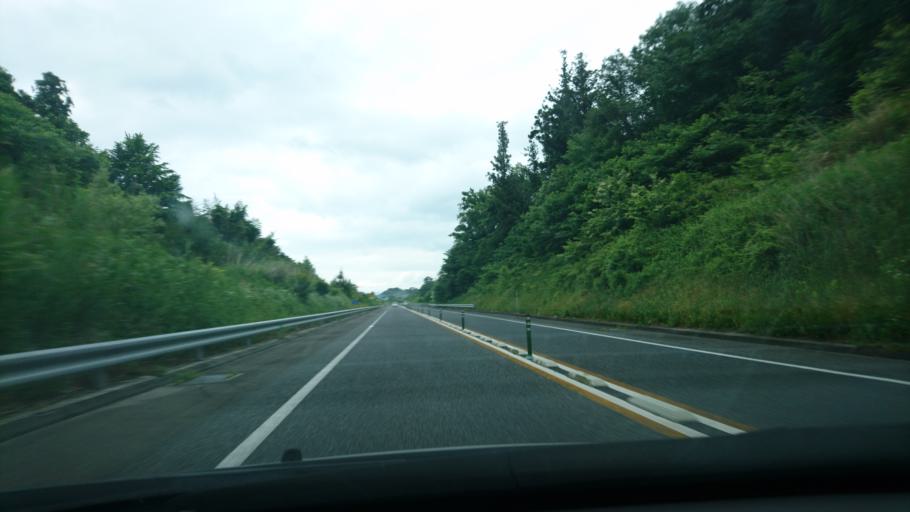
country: JP
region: Iwate
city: Ichinoseki
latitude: 38.7368
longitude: 141.1024
